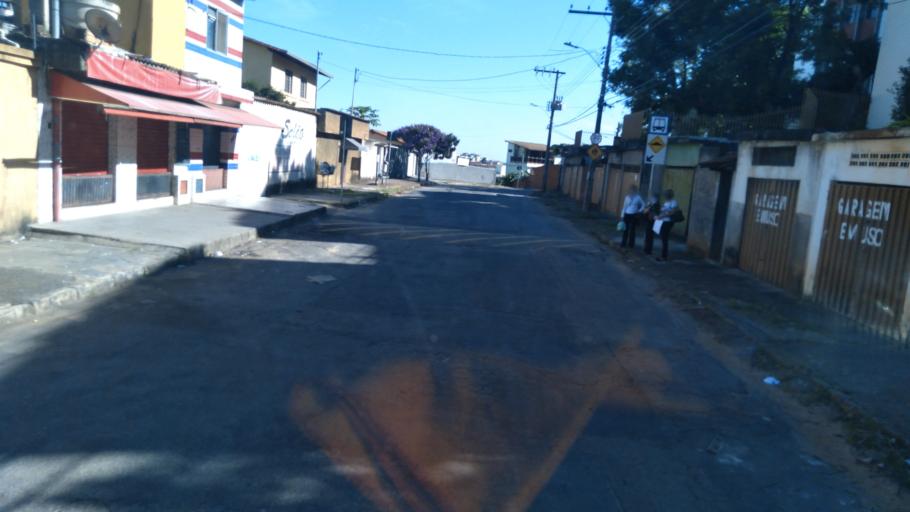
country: BR
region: Minas Gerais
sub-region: Contagem
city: Contagem
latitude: -19.9223
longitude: -44.0077
